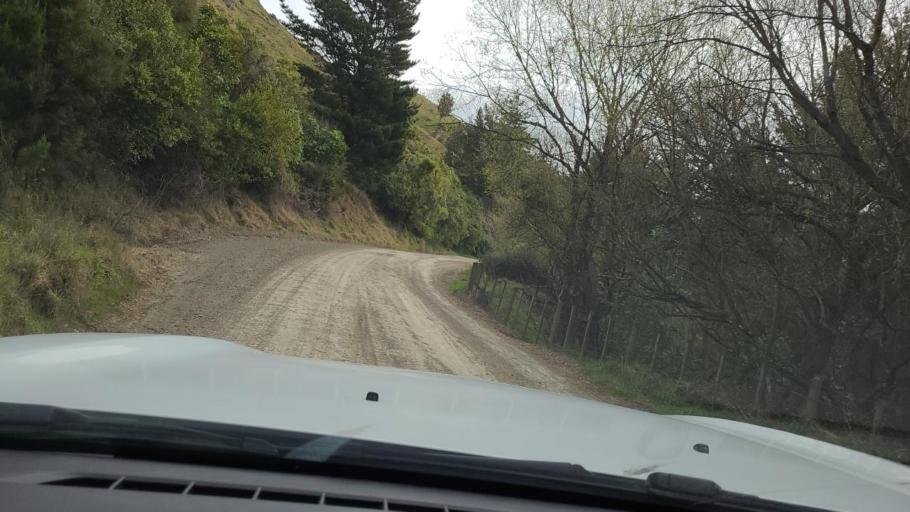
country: NZ
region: Hawke's Bay
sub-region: Napier City
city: Napier
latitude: -39.2817
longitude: 176.8409
